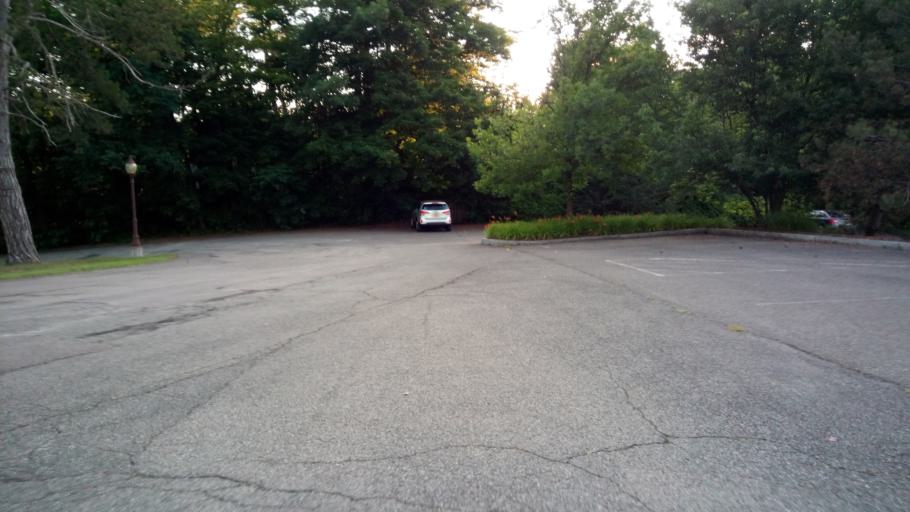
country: US
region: New York
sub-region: Chemung County
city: West Elmira
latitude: 42.0826
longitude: -76.8496
